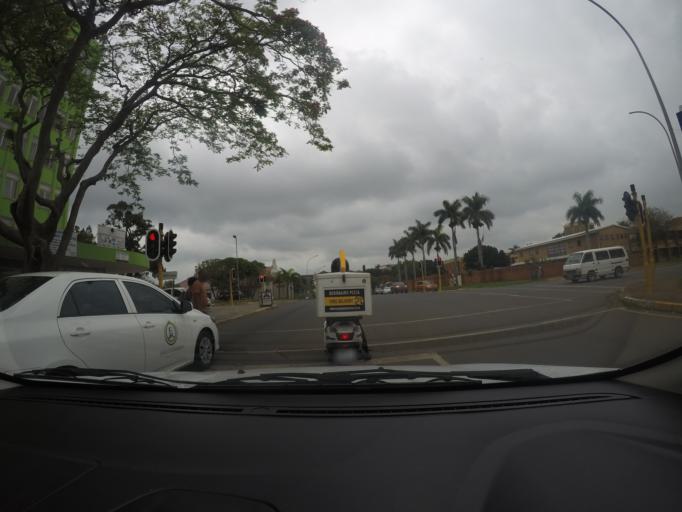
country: ZA
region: KwaZulu-Natal
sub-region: uThungulu District Municipality
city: Empangeni
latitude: -28.7447
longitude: 31.8918
